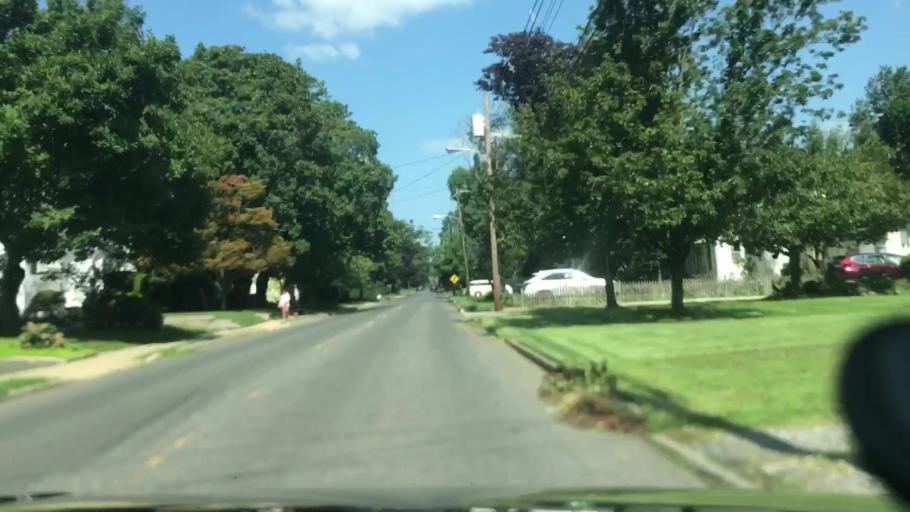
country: US
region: New Jersey
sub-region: Monmouth County
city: Little Silver
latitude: 40.3419
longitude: -74.0449
